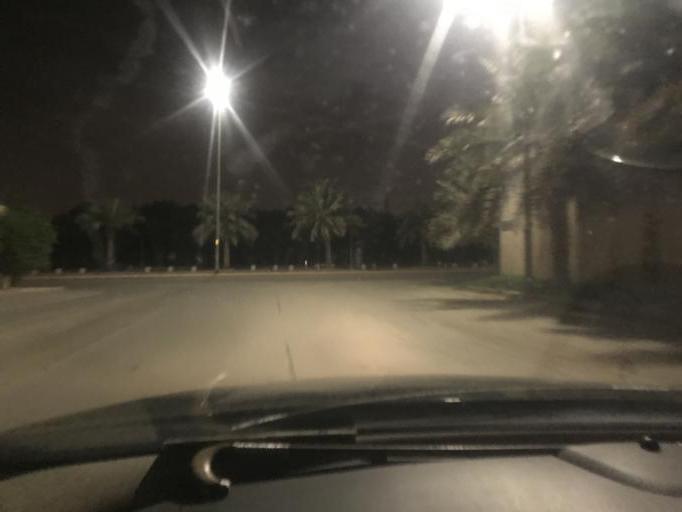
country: SA
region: Ar Riyad
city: Riyadh
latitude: 24.7321
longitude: 46.7773
